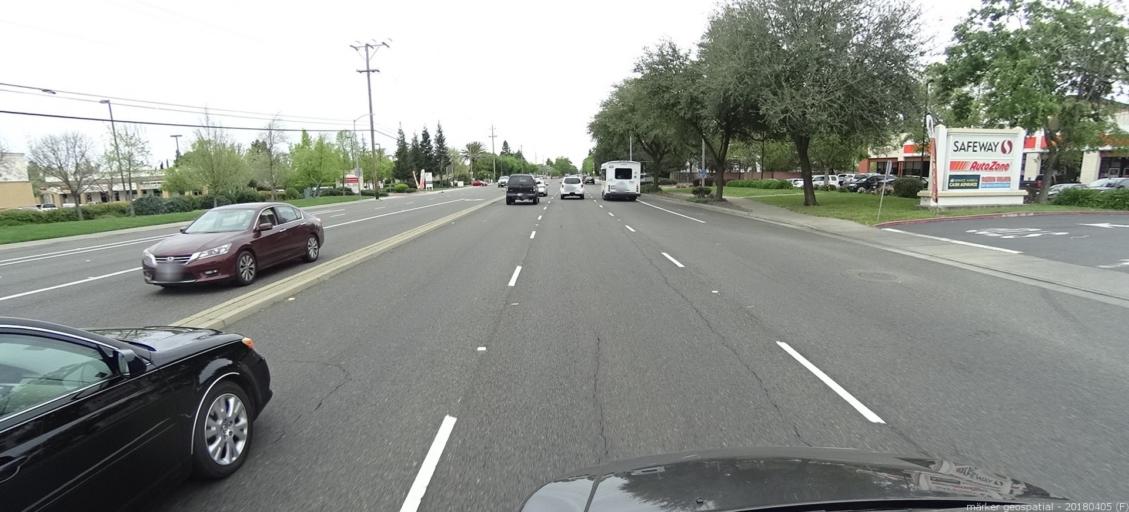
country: US
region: California
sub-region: Sacramento County
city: Laguna
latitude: 38.4237
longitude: -121.4479
